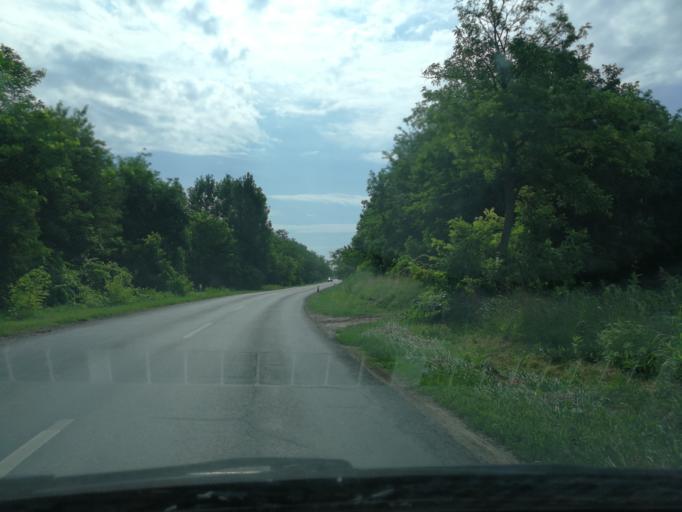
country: HU
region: Bacs-Kiskun
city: Nagybaracska
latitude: 46.0374
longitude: 18.9280
